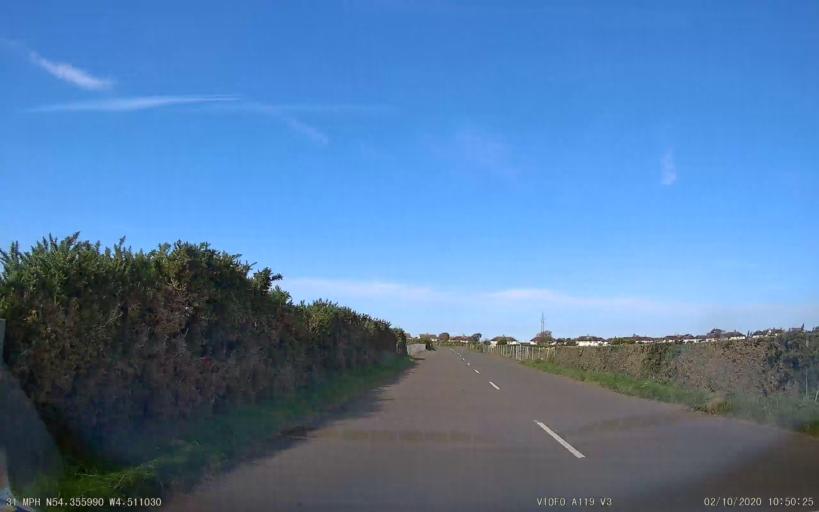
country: IM
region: Ramsey
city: Ramsey
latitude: 54.3560
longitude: -4.5108
